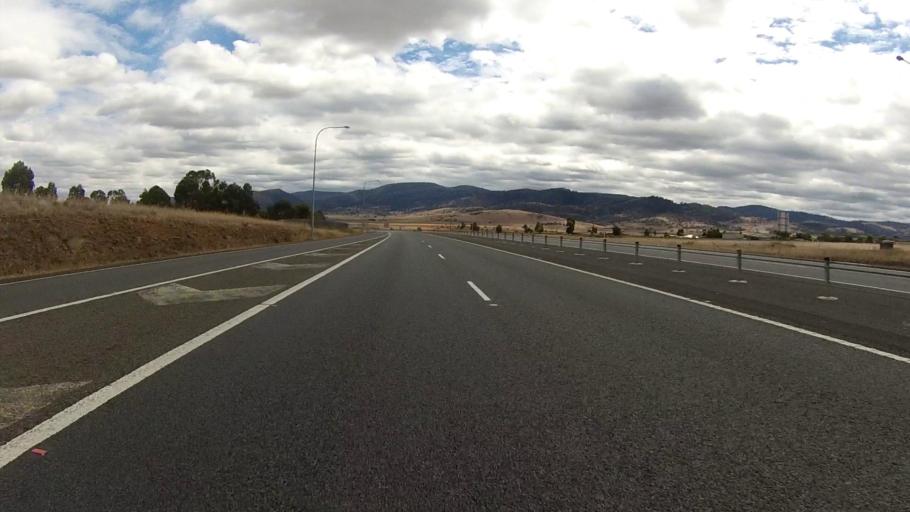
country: AU
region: Tasmania
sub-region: Brighton
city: Bridgewater
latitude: -42.6942
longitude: 147.2778
